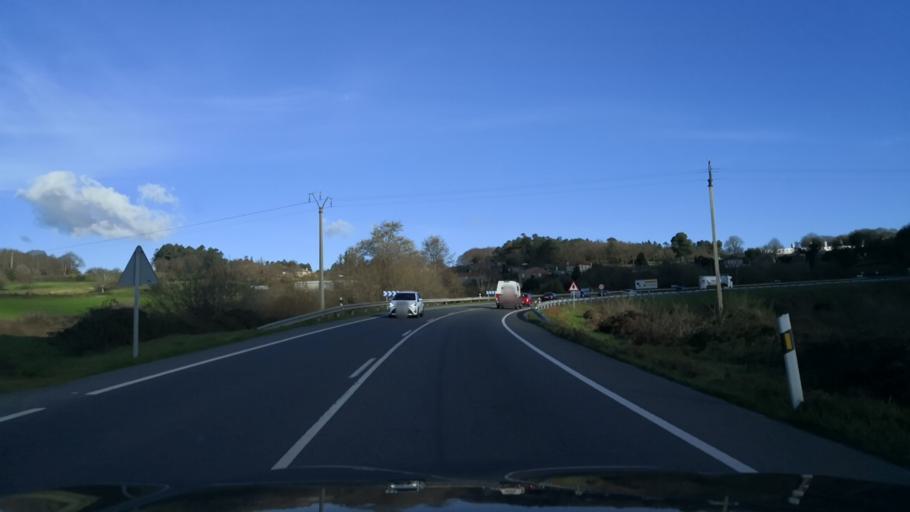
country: ES
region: Galicia
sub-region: Provincia de Pontevedra
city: Silleda
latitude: 42.7065
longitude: -8.2617
